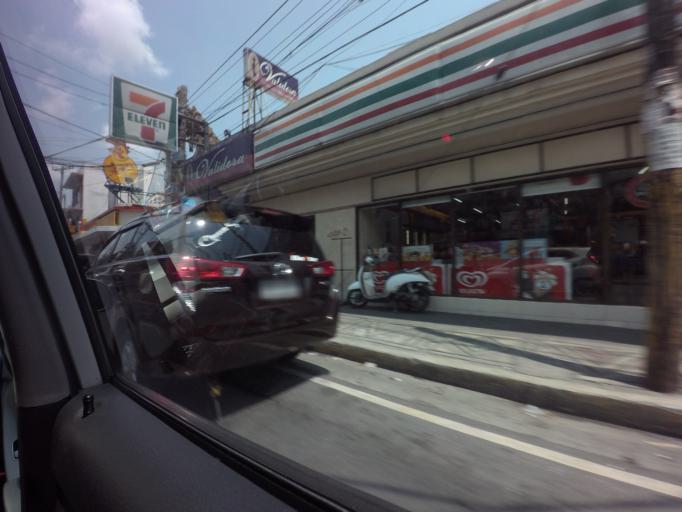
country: PH
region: Metro Manila
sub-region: City of Manila
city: Quiapo
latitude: 14.5928
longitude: 121.0040
